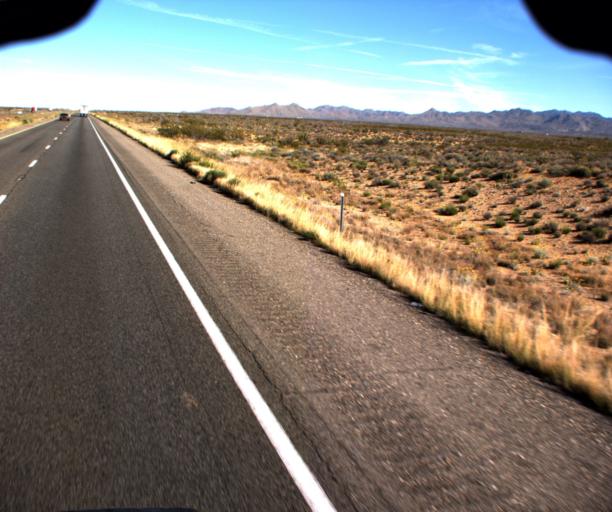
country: US
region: Arizona
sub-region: Mohave County
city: Golden Valley
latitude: 35.3462
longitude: -114.2225
